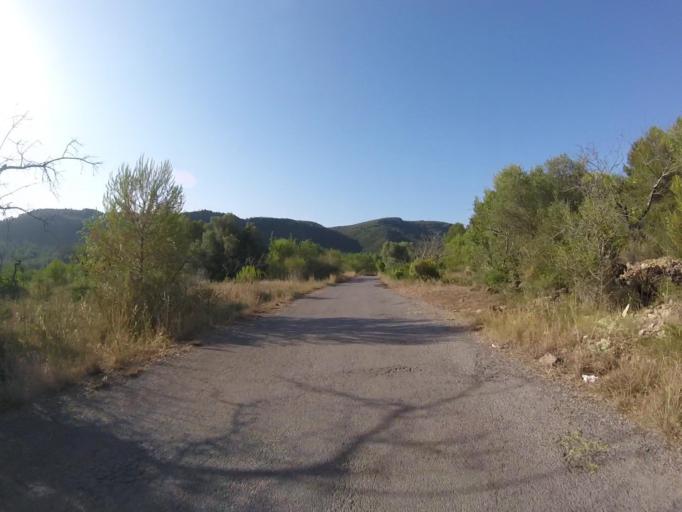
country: ES
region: Valencia
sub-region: Provincia de Castello
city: Cabanes
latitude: 40.1052
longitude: 0.0646
